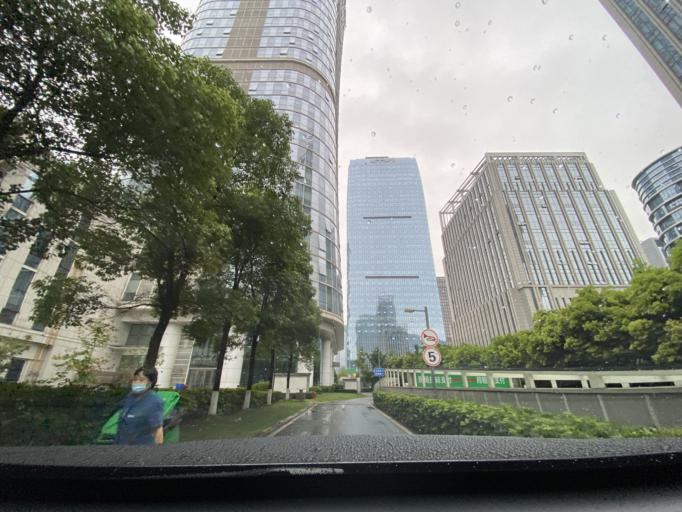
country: CN
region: Sichuan
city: Chengdu
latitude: 30.5436
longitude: 104.0615
